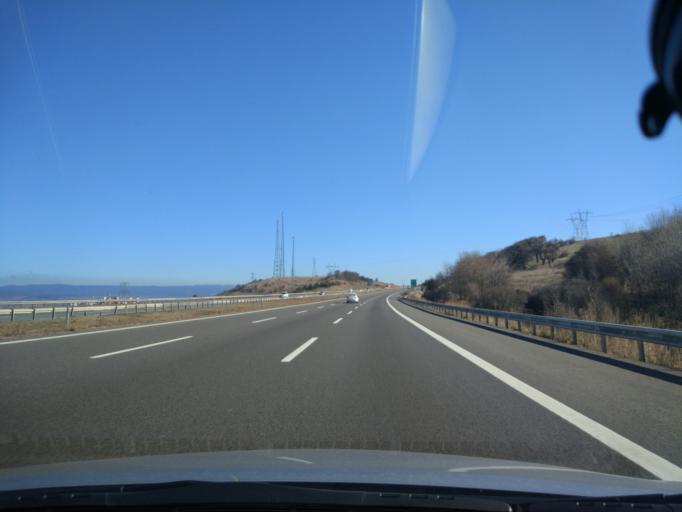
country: TR
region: Bolu
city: Yenicaga
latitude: 40.7653
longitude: 32.0220
